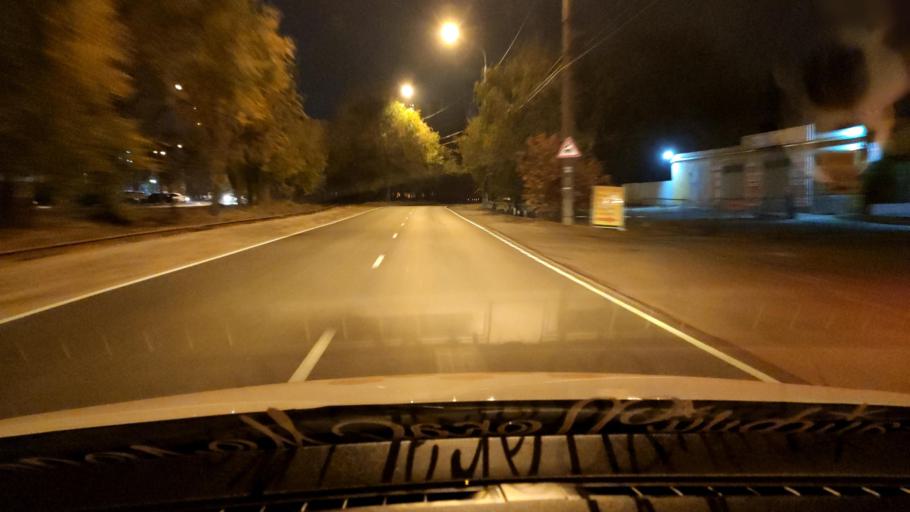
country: RU
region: Voronezj
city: Voronezh
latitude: 51.6801
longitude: 39.1661
